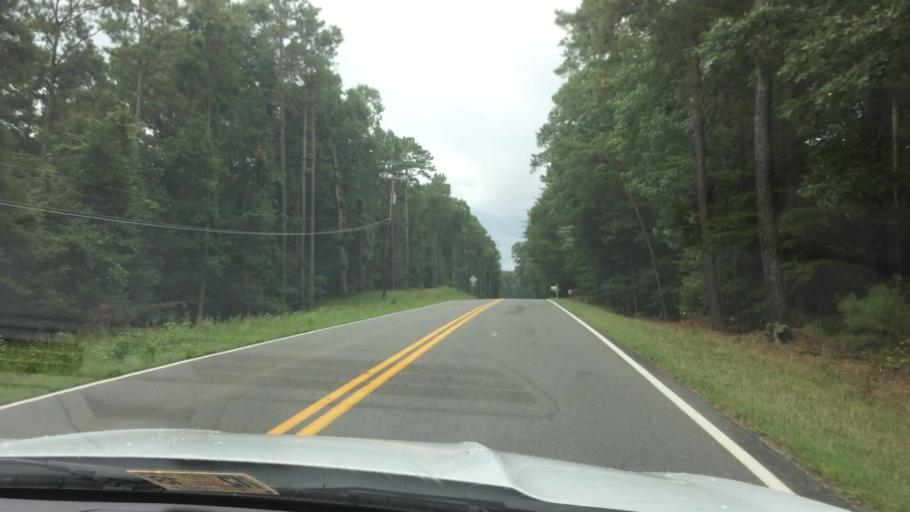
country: US
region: Virginia
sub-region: New Kent County
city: New Kent
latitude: 37.4698
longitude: -77.0331
